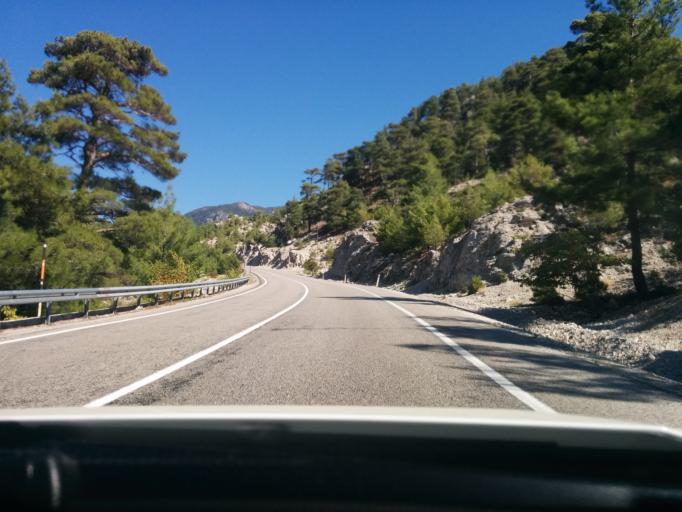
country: TR
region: Mugla
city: Kemer
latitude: 36.7692
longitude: 29.4629
